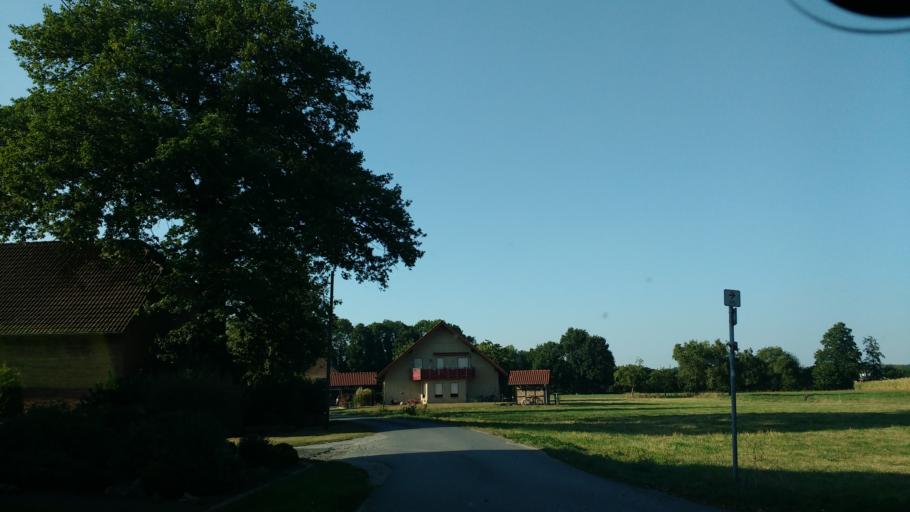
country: DE
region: North Rhine-Westphalia
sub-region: Regierungsbezirk Detmold
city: Delbruck
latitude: 51.7553
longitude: 8.5414
